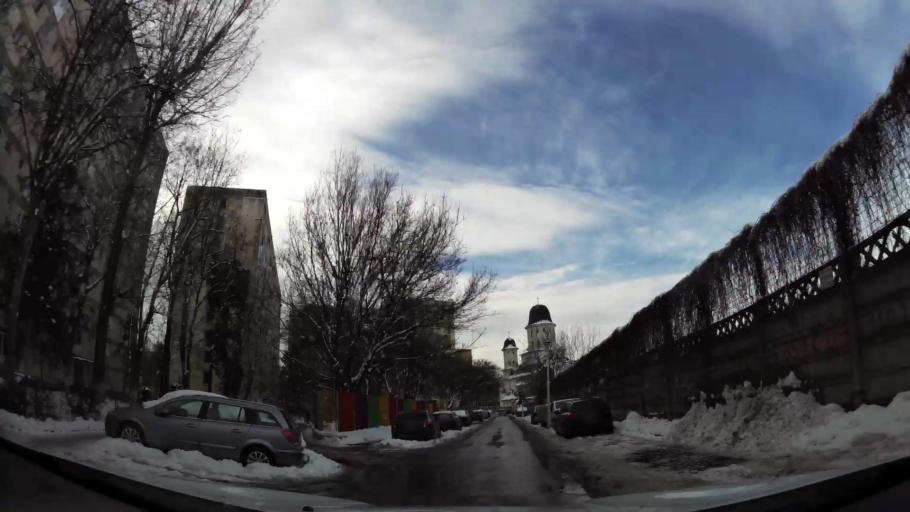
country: RO
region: Ilfov
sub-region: Comuna Popesti-Leordeni
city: Popesti-Leordeni
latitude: 44.3836
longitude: 26.1262
